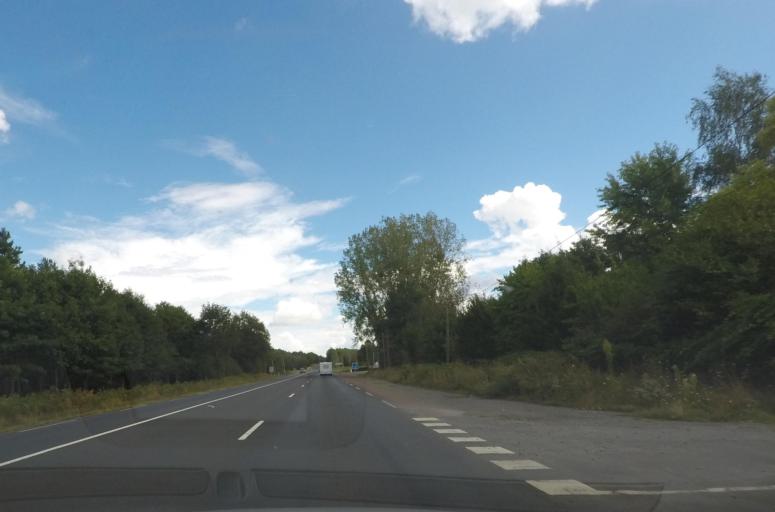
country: FR
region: Pays de la Loire
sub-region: Departement de la Sarthe
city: Parigne-le-Polin
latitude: 47.8436
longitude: 0.0888
